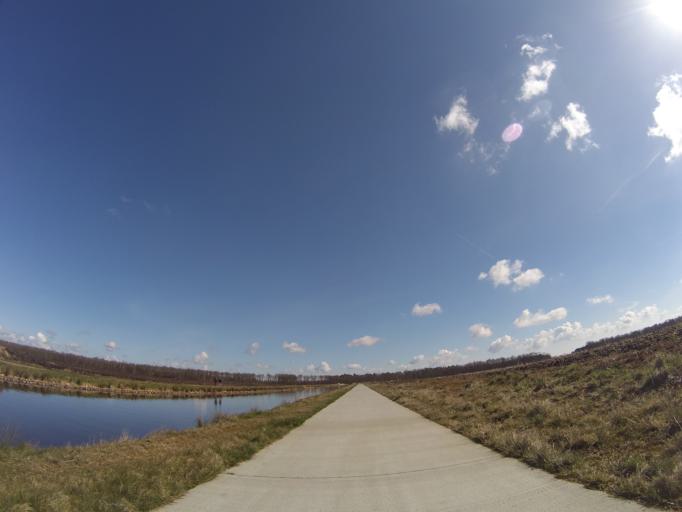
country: NL
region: Drenthe
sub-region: Gemeente Emmen
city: Klazienaveen
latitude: 52.7429
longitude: 6.9808
